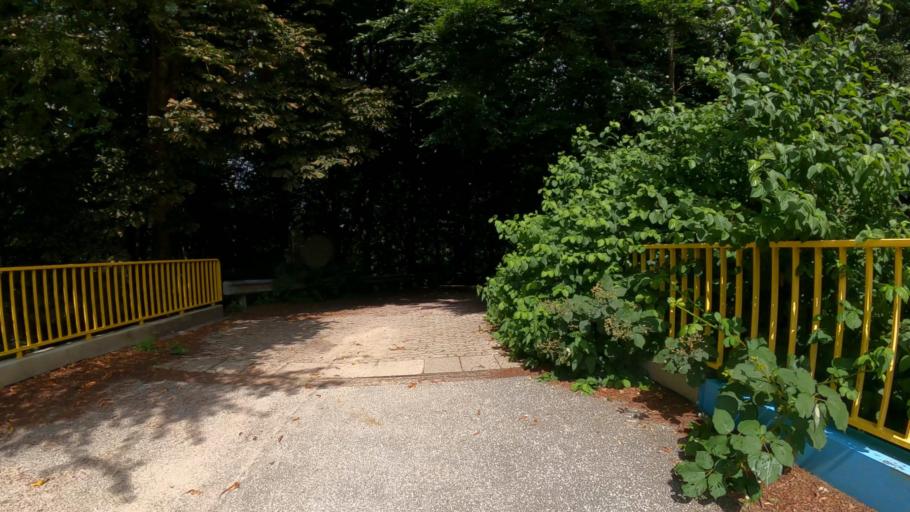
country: DE
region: Hamburg
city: Harburg
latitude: 53.4546
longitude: 9.9239
